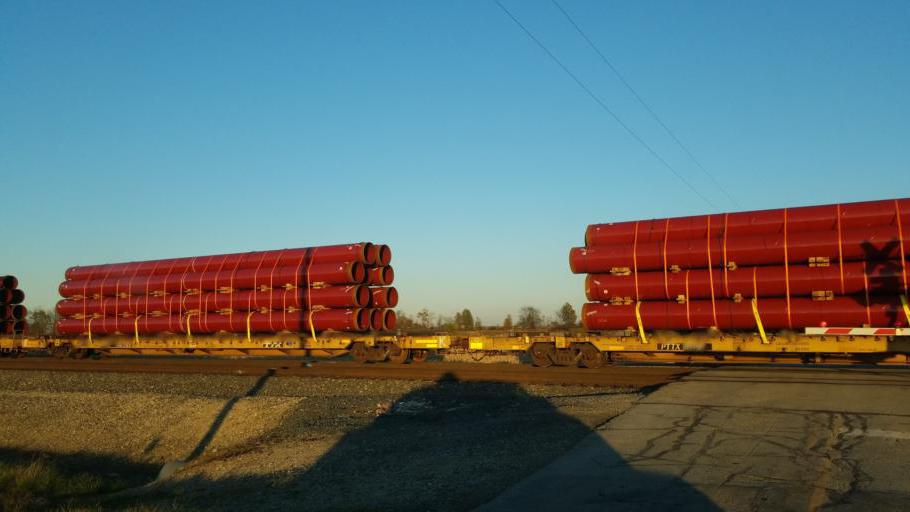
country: US
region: Ohio
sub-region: Huron County
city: Bellevue
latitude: 41.2117
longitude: -82.8699
